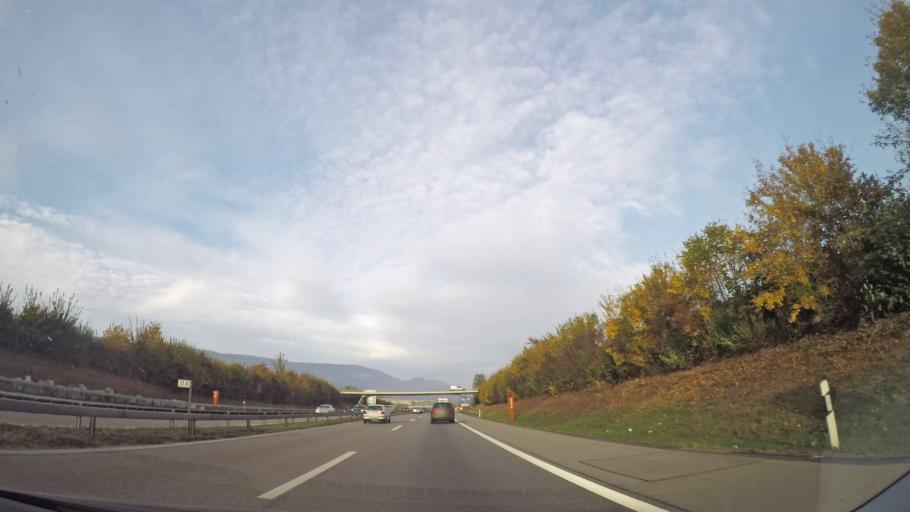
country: CH
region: Solothurn
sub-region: Bezirk Wasseramt
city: Deitingen
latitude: 47.2203
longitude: 7.6061
